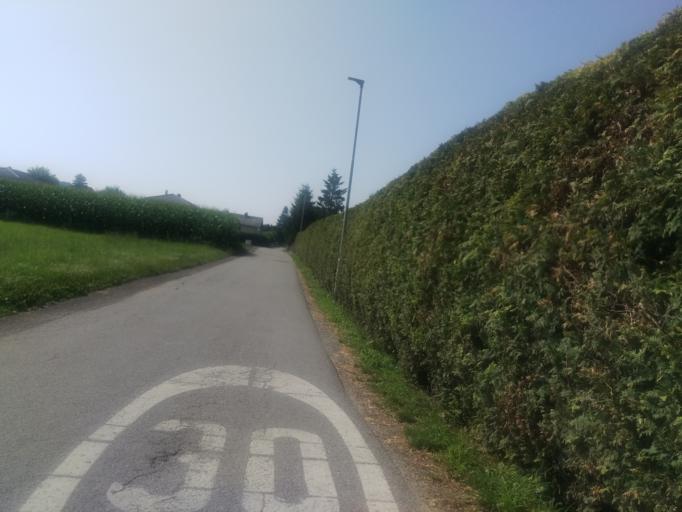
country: AT
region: Styria
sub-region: Politischer Bezirk Graz-Umgebung
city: Gossendorf
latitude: 46.9801
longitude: 15.4906
